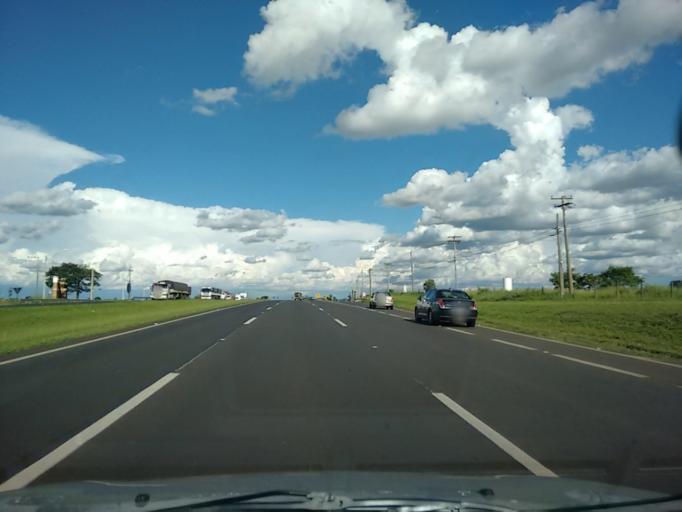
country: BR
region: Sao Paulo
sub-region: Sao Carlos
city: Sao Carlos
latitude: -21.9756
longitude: -47.9354
